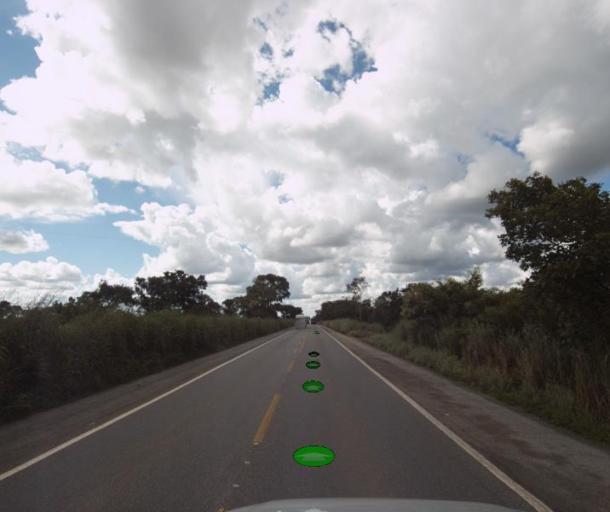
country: BR
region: Goias
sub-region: Porangatu
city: Porangatu
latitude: -13.3712
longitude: -49.1259
